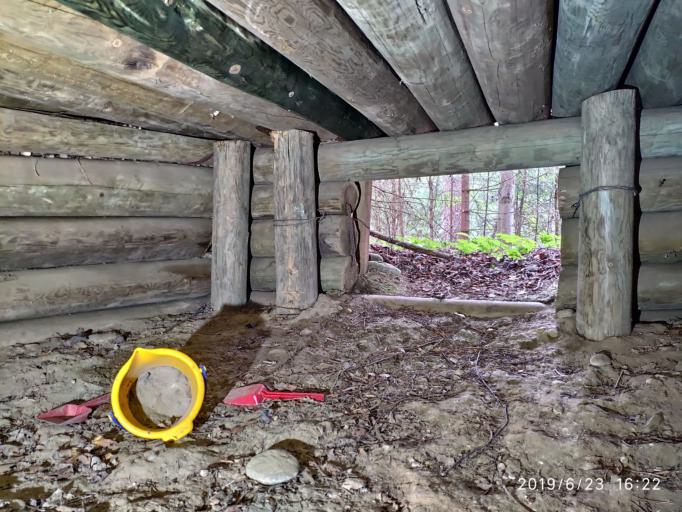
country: NO
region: Buskerud
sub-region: Ringerike
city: Honefoss
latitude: 60.1533
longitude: 10.3135
